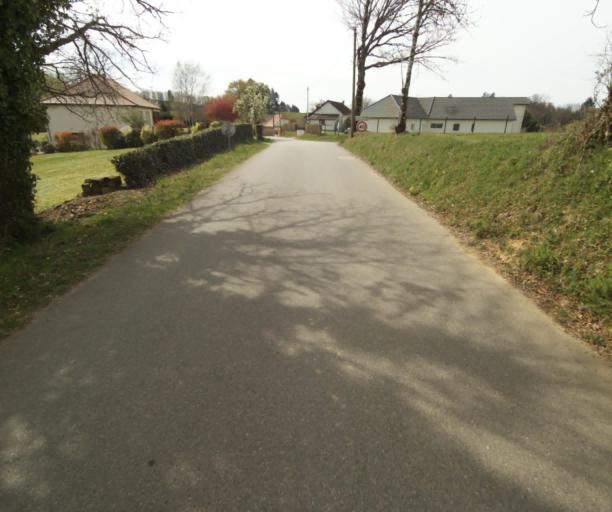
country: FR
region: Limousin
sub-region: Departement de la Correze
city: Naves
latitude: 45.3030
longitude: 1.7643
